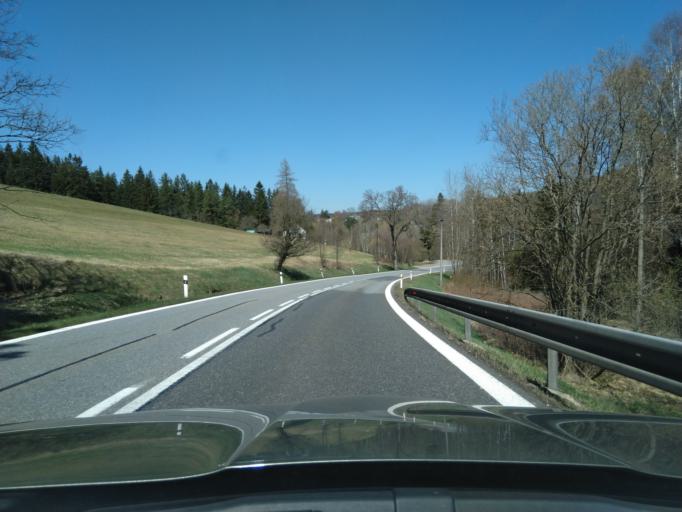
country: CZ
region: Jihocesky
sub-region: Okres Prachatice
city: Vimperk
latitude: 49.0235
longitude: 13.7668
